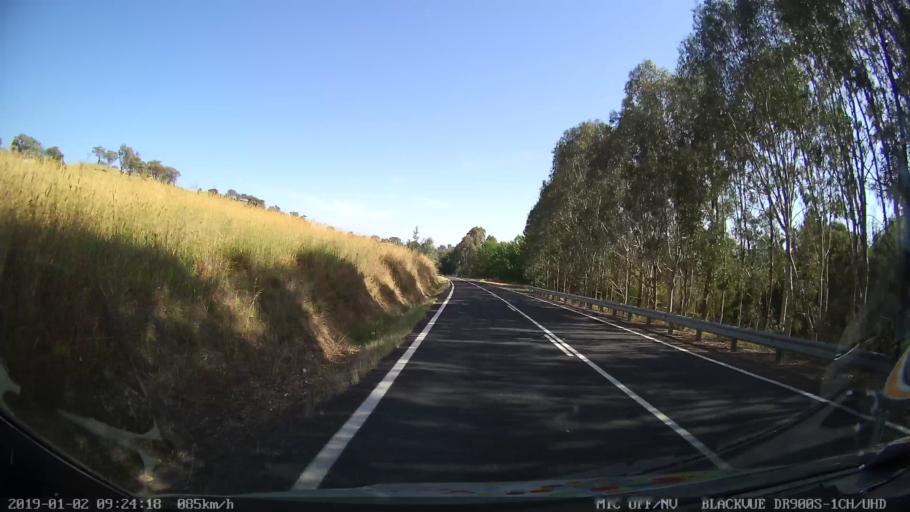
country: AU
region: New South Wales
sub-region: Tumut Shire
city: Tumut
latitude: -35.3789
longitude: 148.2921
